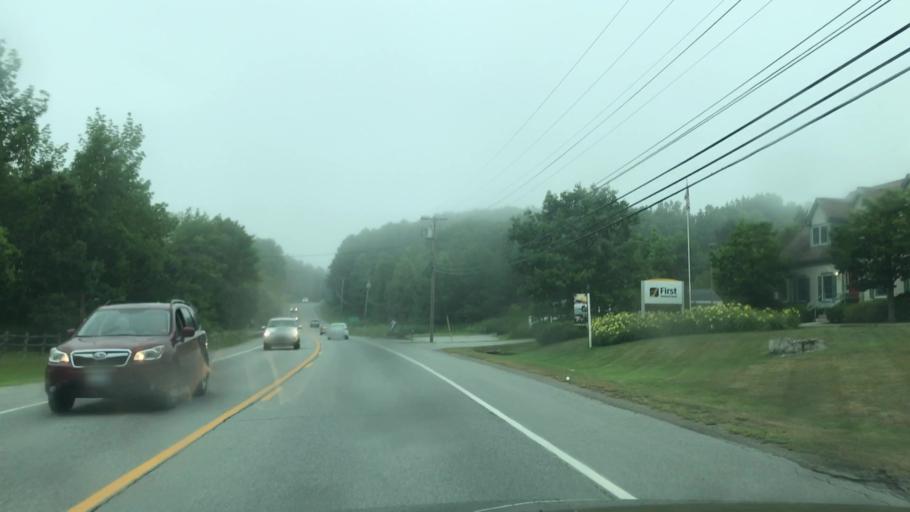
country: US
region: Maine
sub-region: Knox County
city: Rockport
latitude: 44.1925
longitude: -69.0795
